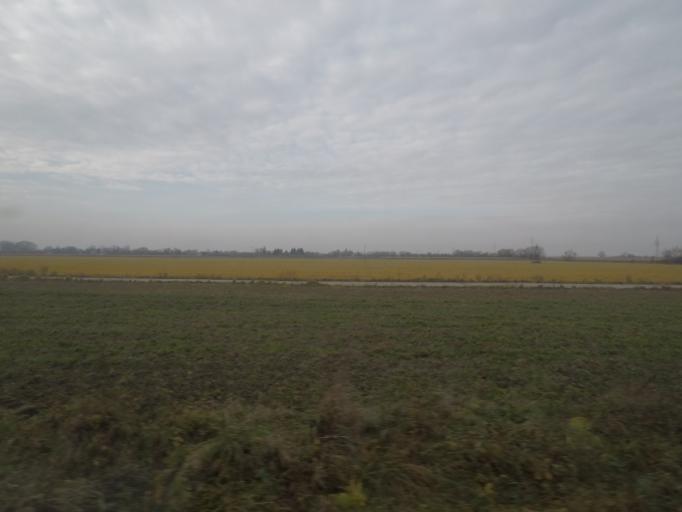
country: PL
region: Subcarpathian Voivodeship
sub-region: Powiat przemyski
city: Medyka
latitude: 49.7932
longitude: 22.8885
